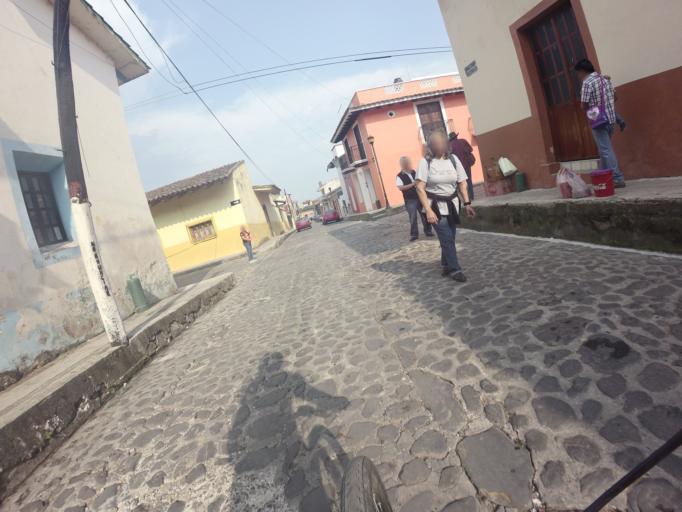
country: MX
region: Veracruz
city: Xico
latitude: 19.4219
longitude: -97.0100
